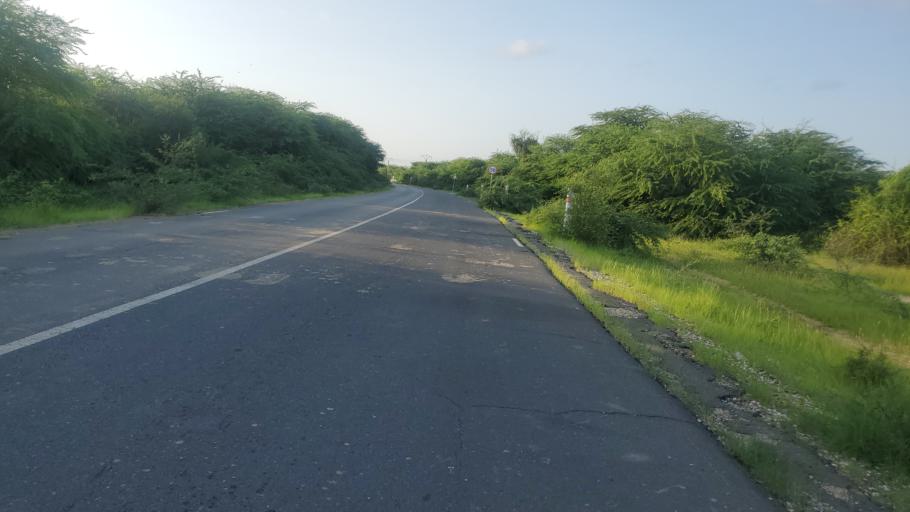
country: SN
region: Saint-Louis
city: Saint-Louis
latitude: 16.1964
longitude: -16.4095
